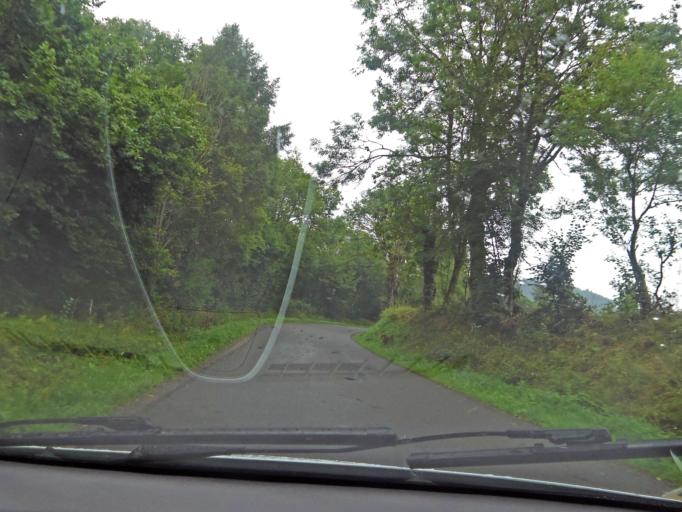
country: FR
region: Auvergne
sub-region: Departement du Puy-de-Dome
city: Saint-Genes-Champanelle
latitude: 45.7287
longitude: 2.9853
